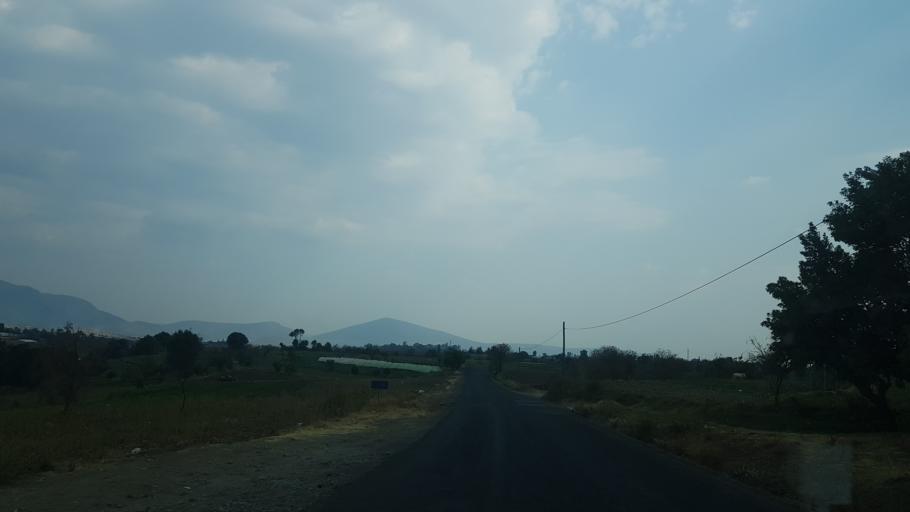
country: MX
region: Puebla
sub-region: Santa Isabel Cholula
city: San Martin Tlamapa
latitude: 18.9656
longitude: -98.3958
